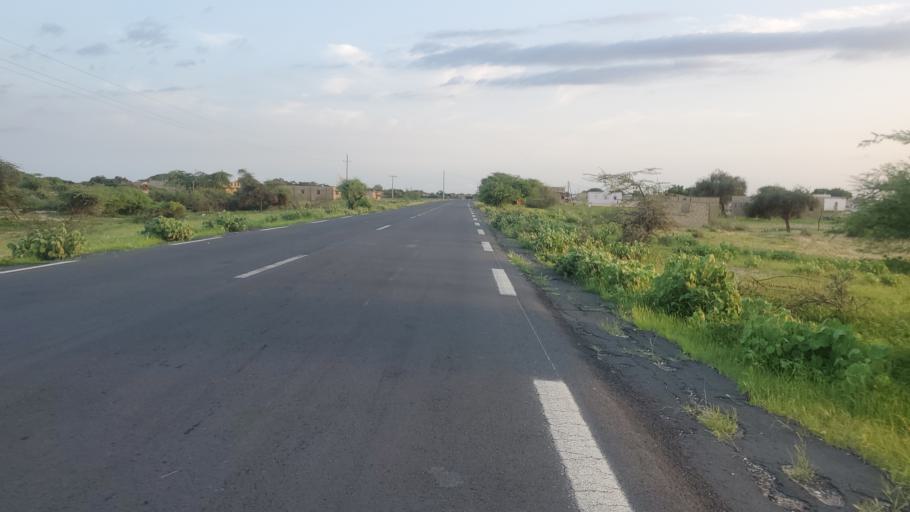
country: SN
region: Saint-Louis
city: Saint-Louis
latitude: 16.1440
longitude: -16.4097
